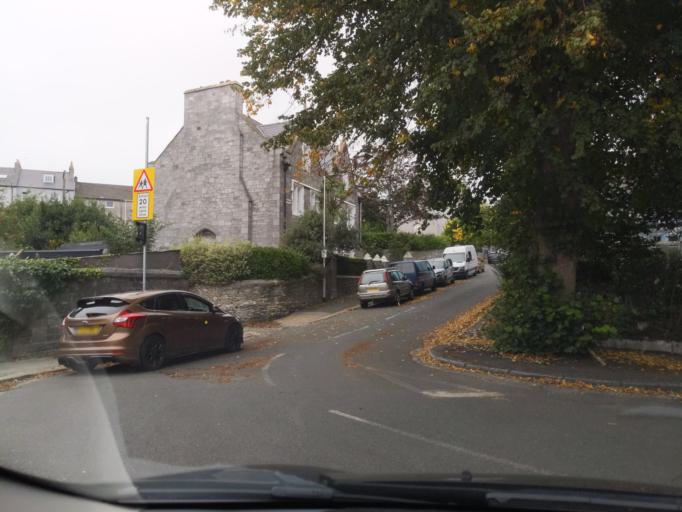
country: GB
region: England
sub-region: Cornwall
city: Millbrook
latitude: 50.3755
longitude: -4.1645
